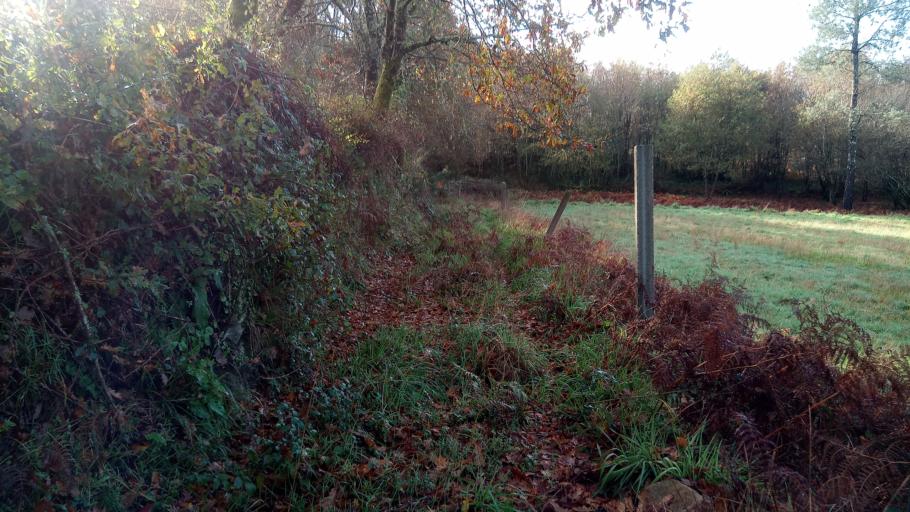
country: PT
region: Viana do Castelo
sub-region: Paredes de Coura
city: Paredes de Coura
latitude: 41.8965
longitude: -8.6158
